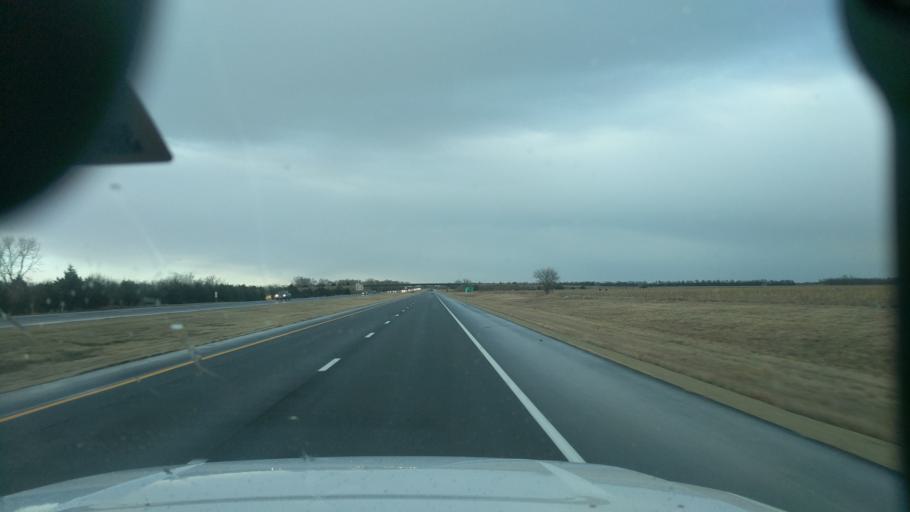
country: US
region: Kansas
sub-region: Harvey County
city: Newton
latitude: 37.9652
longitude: -97.3272
